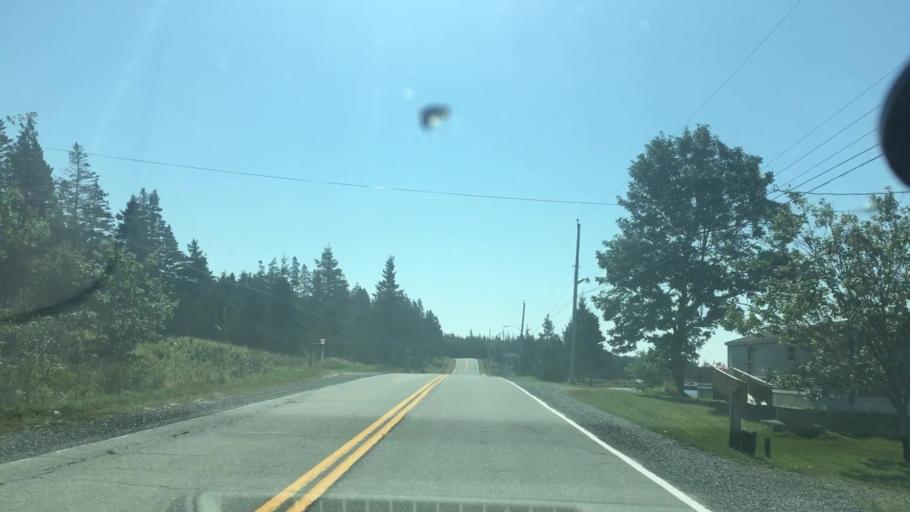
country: CA
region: Nova Scotia
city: New Glasgow
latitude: 44.9144
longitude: -62.3809
